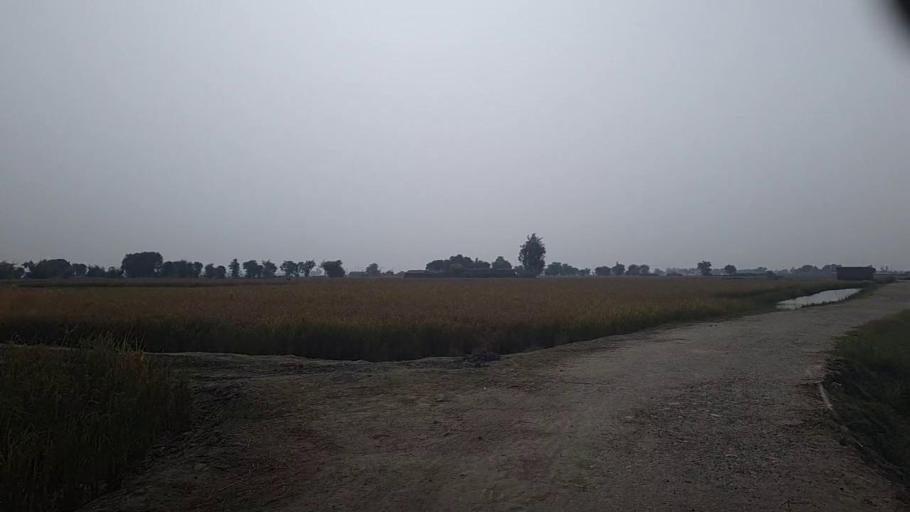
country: PK
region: Sindh
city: Kashmor
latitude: 28.3916
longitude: 69.4262
